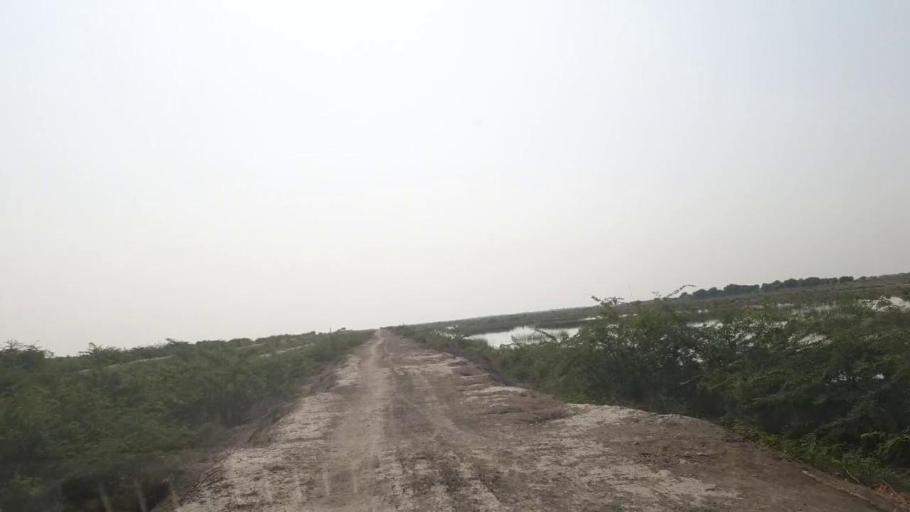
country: PK
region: Sindh
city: Kadhan
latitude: 24.3917
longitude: 68.9027
